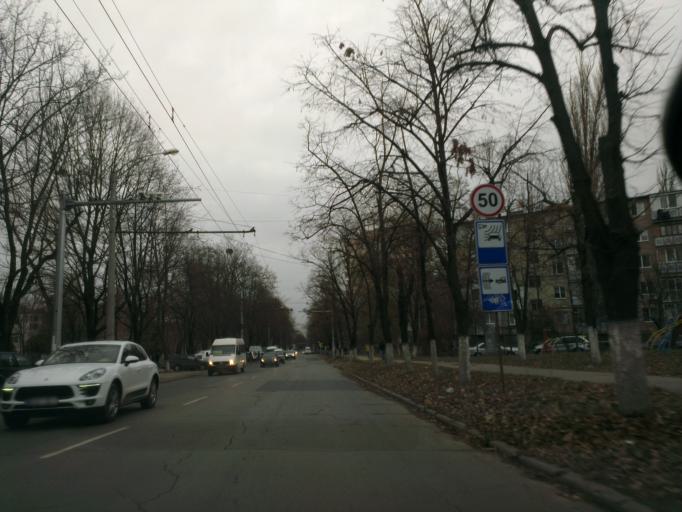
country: MD
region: Chisinau
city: Chisinau
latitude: 46.9910
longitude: 28.8456
